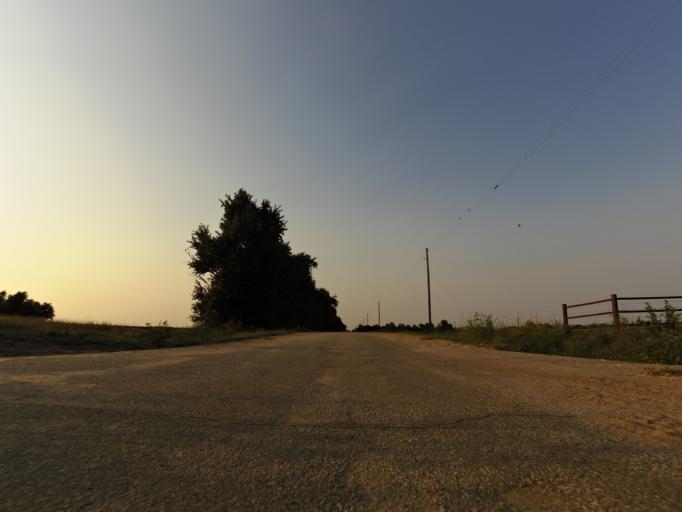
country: US
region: Kansas
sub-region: Reno County
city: South Hutchinson
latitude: 37.9939
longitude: -97.9956
